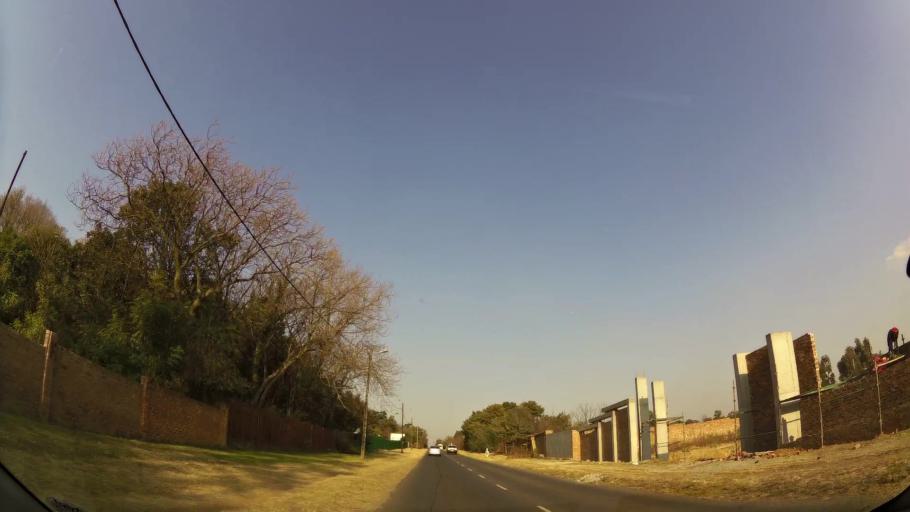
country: ZA
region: Gauteng
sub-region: Ekurhuleni Metropolitan Municipality
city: Benoni
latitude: -26.1443
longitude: 28.3583
